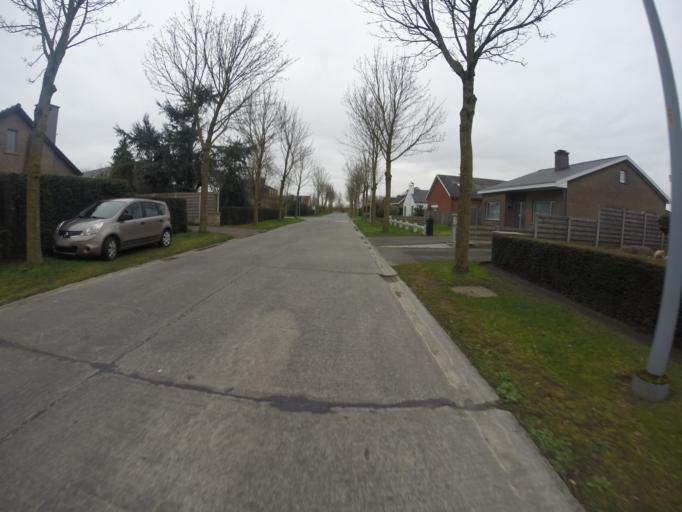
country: BE
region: Flanders
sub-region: Provincie Oost-Vlaanderen
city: Aalter
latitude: 51.1111
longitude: 3.4381
